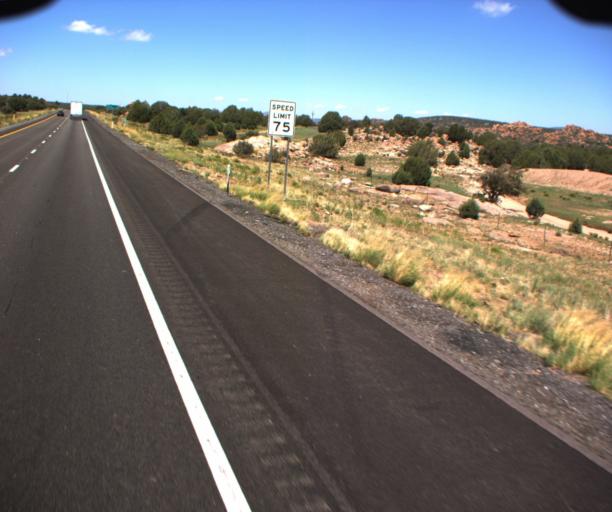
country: US
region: Arizona
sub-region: Mohave County
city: Peach Springs
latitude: 35.1909
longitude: -113.3771
